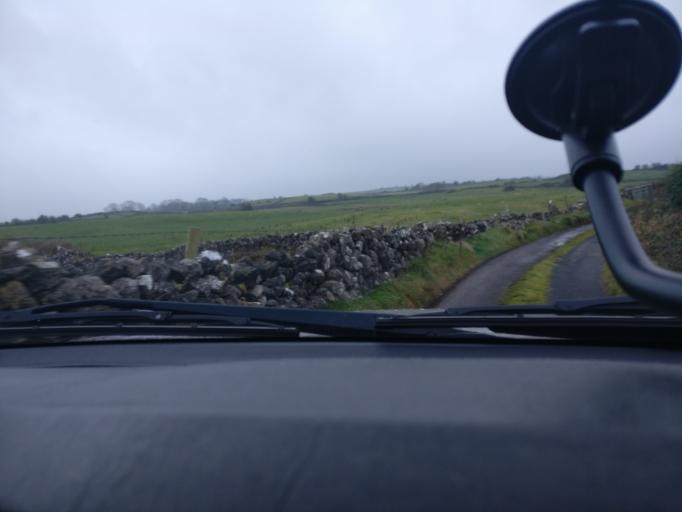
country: IE
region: Connaught
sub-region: County Galway
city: Loughrea
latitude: 53.2117
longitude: -8.5459
